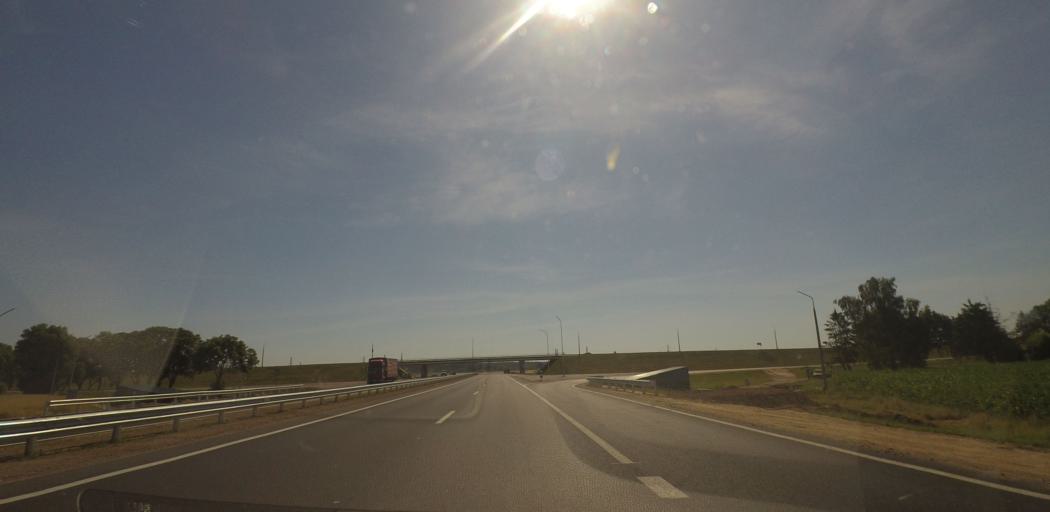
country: BY
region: Grodnenskaya
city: Skidal'
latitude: 53.5788
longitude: 24.2417
